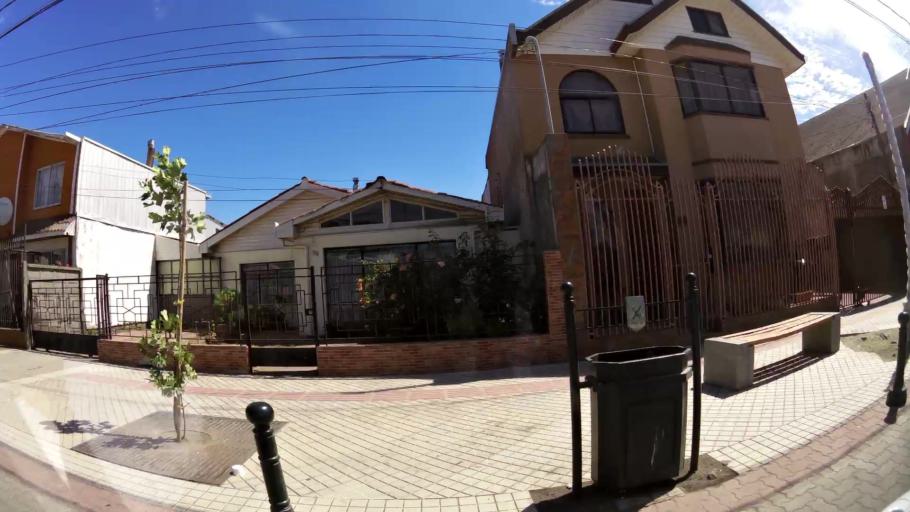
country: CL
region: Biobio
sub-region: Provincia de Concepcion
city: Penco
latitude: -36.7365
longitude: -72.9942
